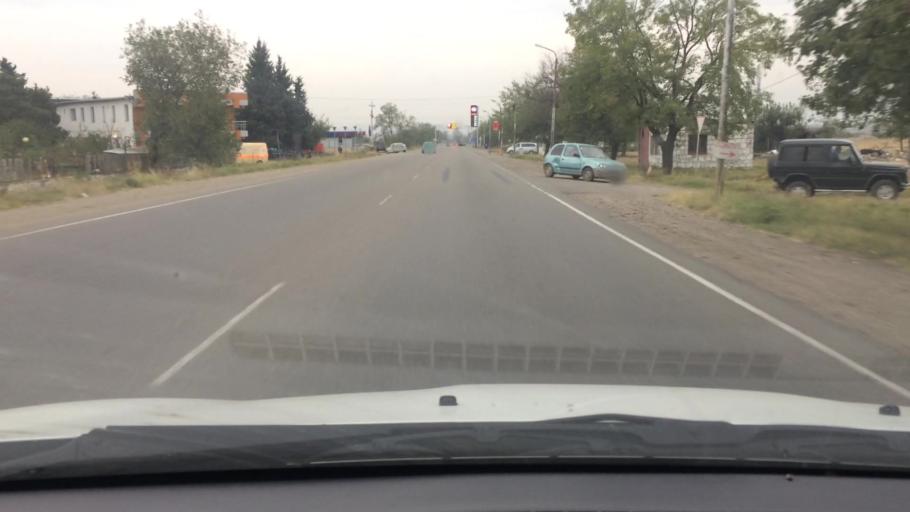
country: GE
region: Kvemo Kartli
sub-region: Marneuli
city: Marneuli
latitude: 41.5758
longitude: 44.7747
